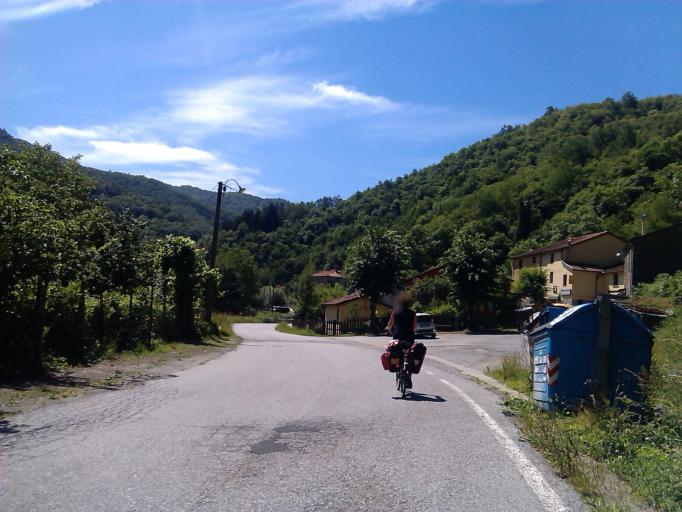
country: IT
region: Tuscany
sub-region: Provincia di Pistoia
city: Sambuca Pistoiese
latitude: 44.0796
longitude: 11.0491
